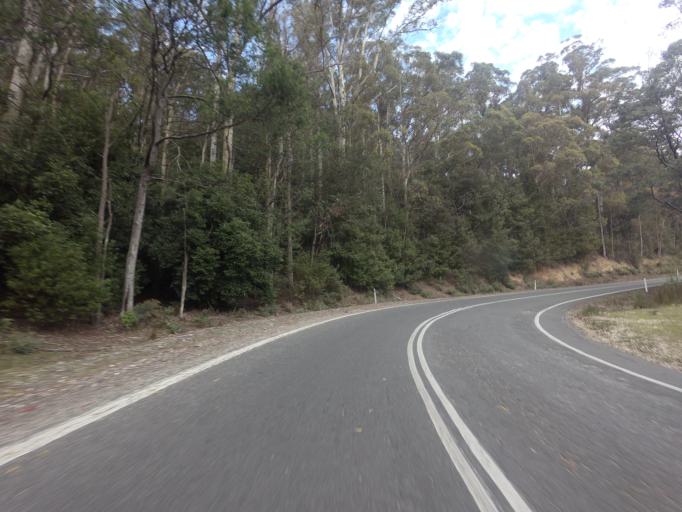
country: AU
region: Tasmania
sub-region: Meander Valley
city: Deloraine
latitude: -41.6460
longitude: 146.7217
